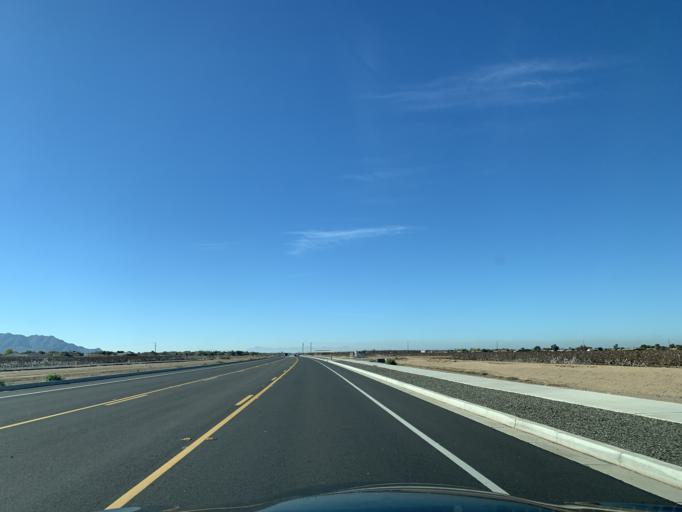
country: US
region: Arizona
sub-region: Maricopa County
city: Queen Creek
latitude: 33.2194
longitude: -111.6118
